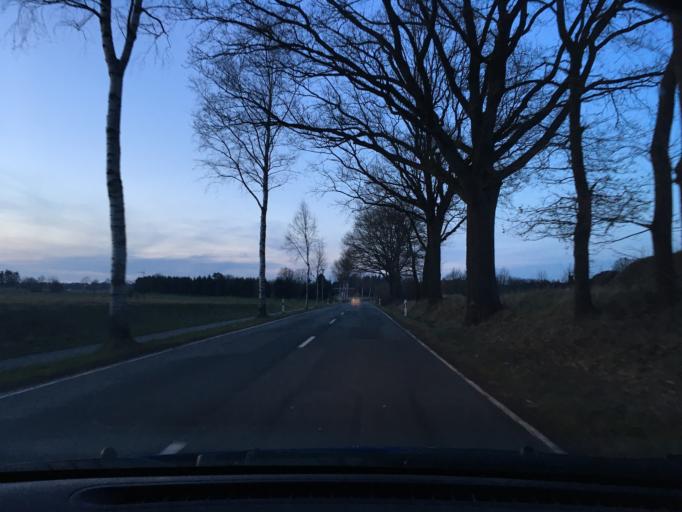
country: DE
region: Lower Saxony
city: Egestorf
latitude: 53.1843
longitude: 10.0629
